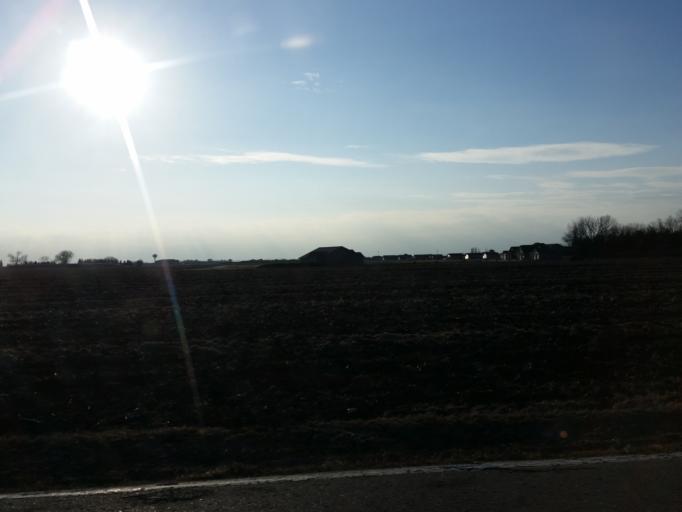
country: US
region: North Dakota
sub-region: Grand Forks County
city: Grand Forks
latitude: 47.8638
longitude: -97.0290
